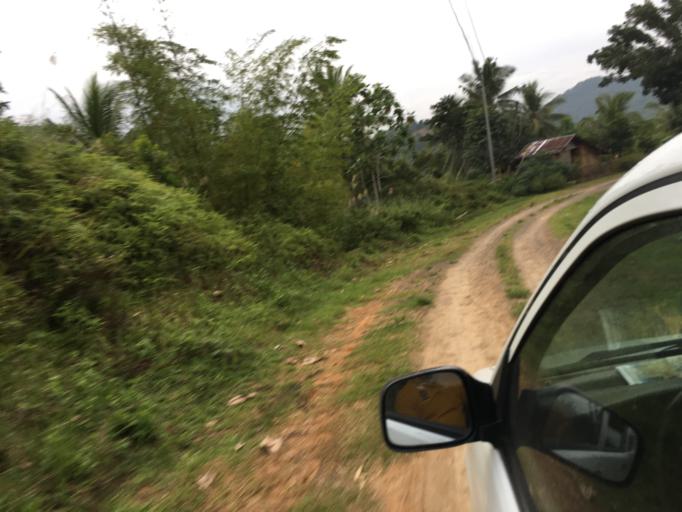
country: PH
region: Western Visayas
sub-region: Province of Aklan
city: Lupo
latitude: 11.4843
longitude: 122.5046
